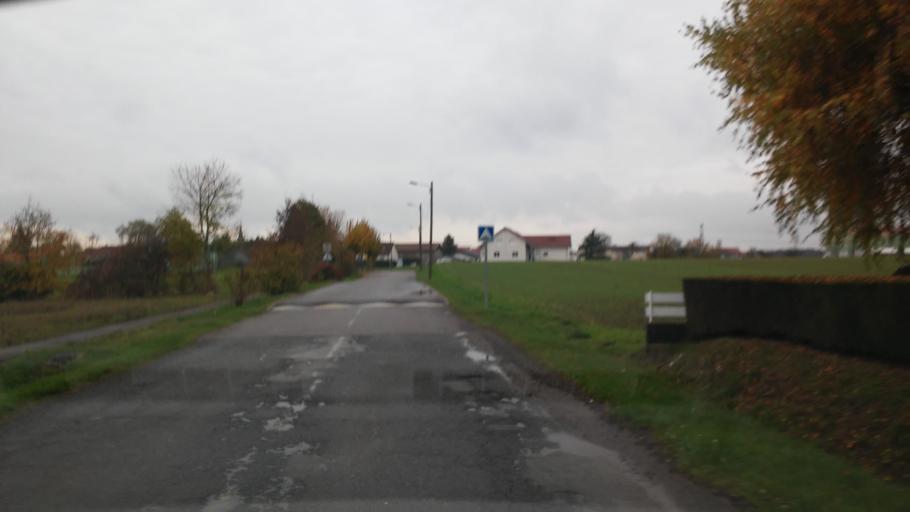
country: FR
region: Lorraine
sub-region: Departement de la Moselle
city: Vigy
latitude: 49.1866
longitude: 6.3321
